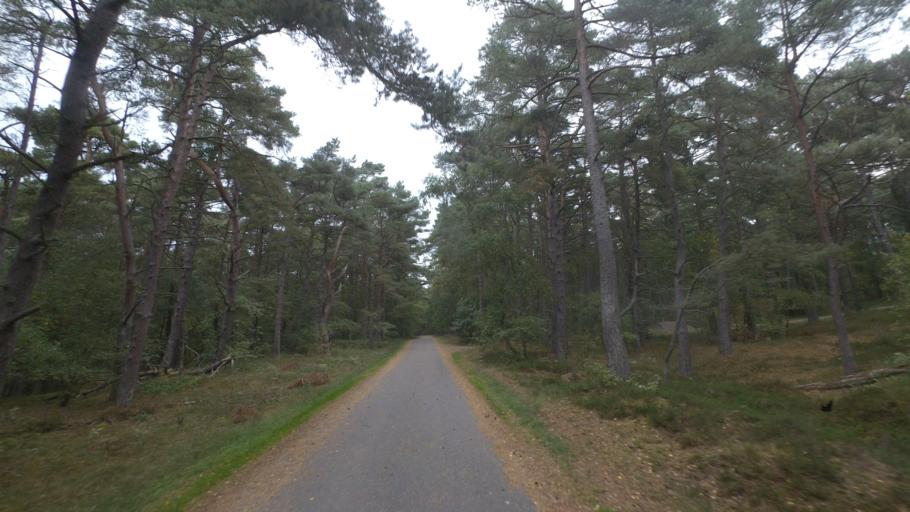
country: DK
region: Capital Region
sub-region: Bornholm Kommune
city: Nexo
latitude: 54.9973
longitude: 15.0385
